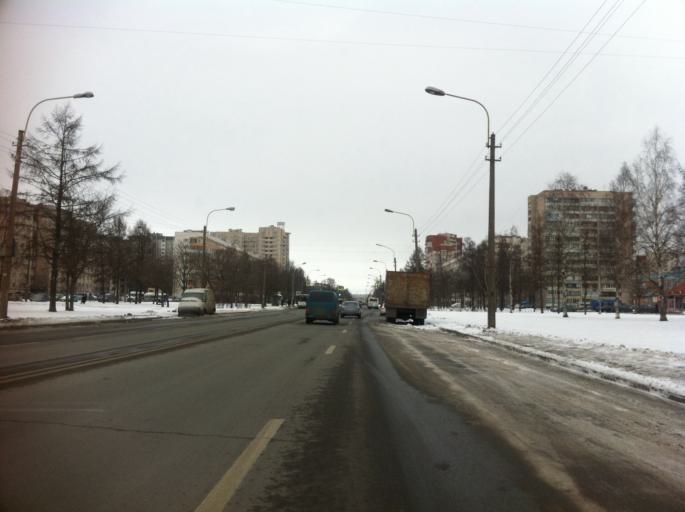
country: RU
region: St.-Petersburg
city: Uritsk
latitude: 59.8277
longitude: 30.1759
